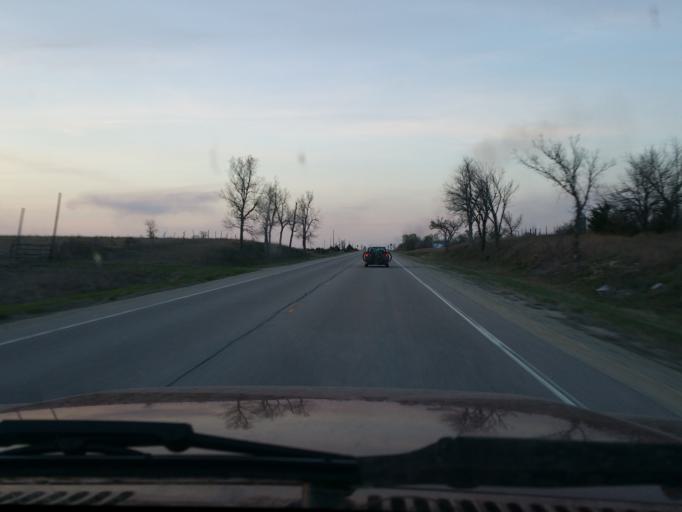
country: US
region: Kansas
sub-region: Riley County
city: Ogden
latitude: 39.3441
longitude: -96.7564
